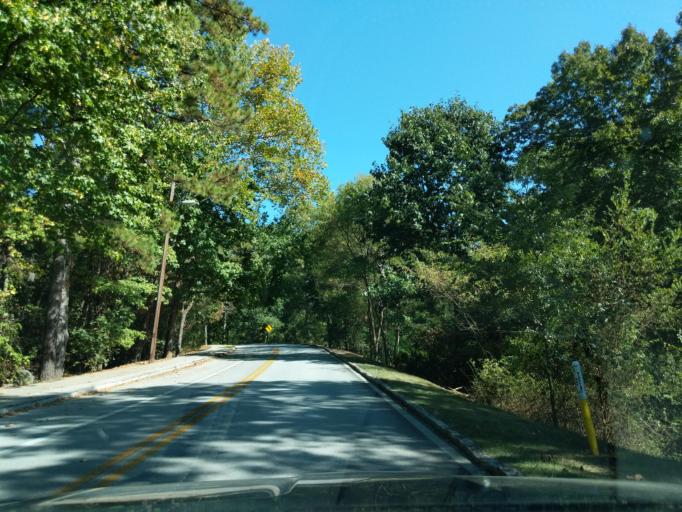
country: US
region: Georgia
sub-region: DeKalb County
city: Stone Mountain
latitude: 33.7990
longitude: -84.1366
